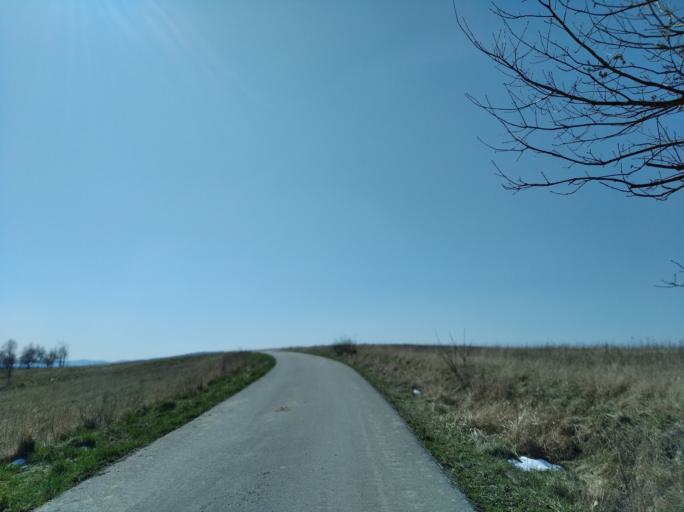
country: PL
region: Subcarpathian Voivodeship
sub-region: Powiat strzyzowski
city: Strzyzow
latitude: 49.8555
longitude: 21.8151
